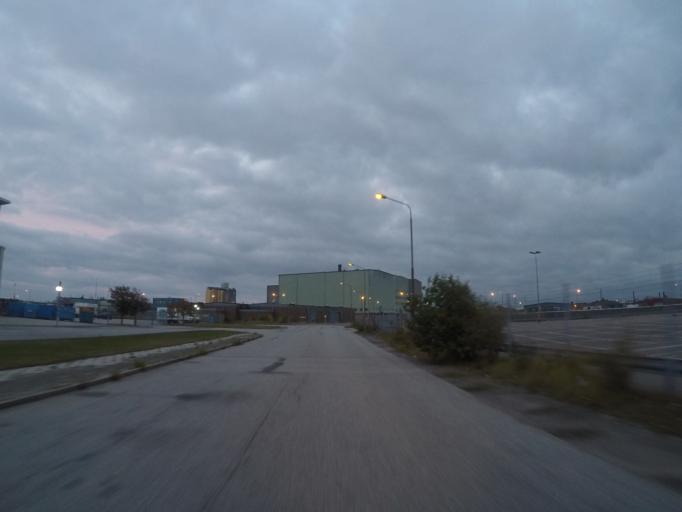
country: SE
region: Skane
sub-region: Malmo
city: Malmoe
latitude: 55.6232
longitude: 13.0151
